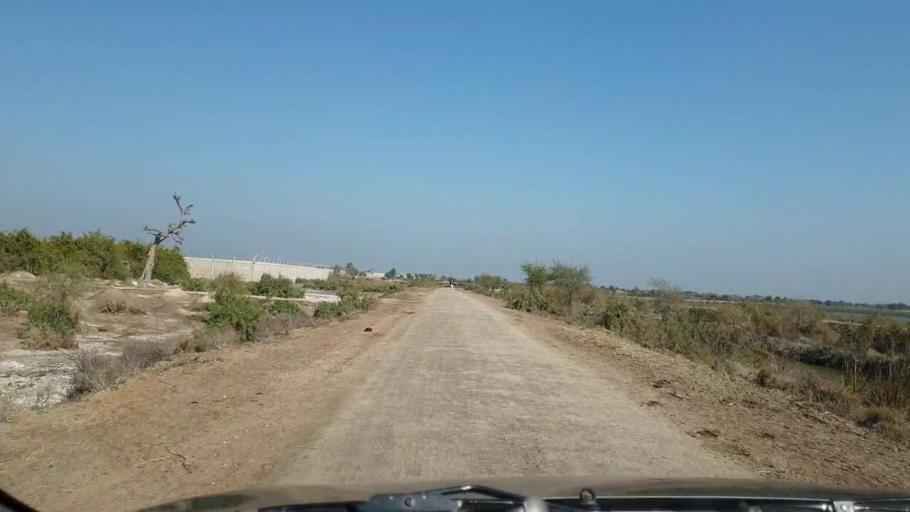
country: PK
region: Sindh
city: Sinjhoro
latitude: 25.9392
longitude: 68.7519
